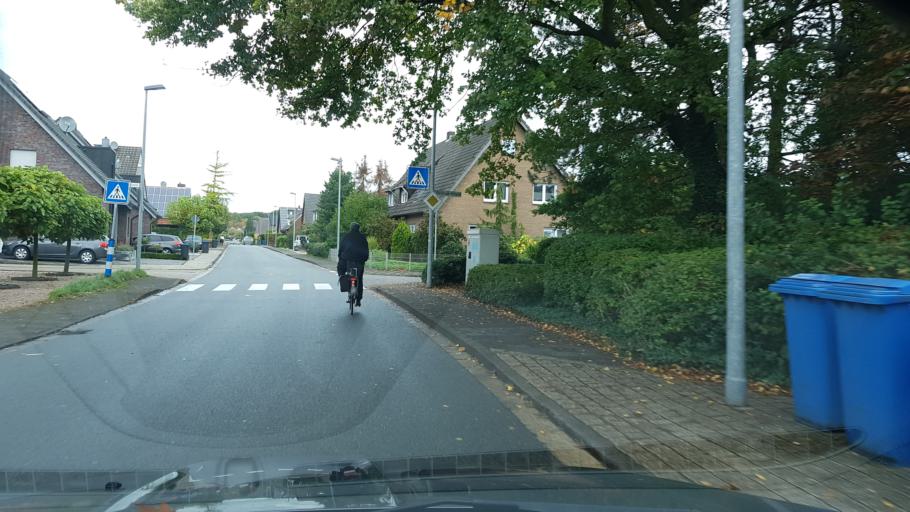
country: DE
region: North Rhine-Westphalia
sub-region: Regierungsbezirk Munster
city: Rhede
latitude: 51.8334
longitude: 6.6867
